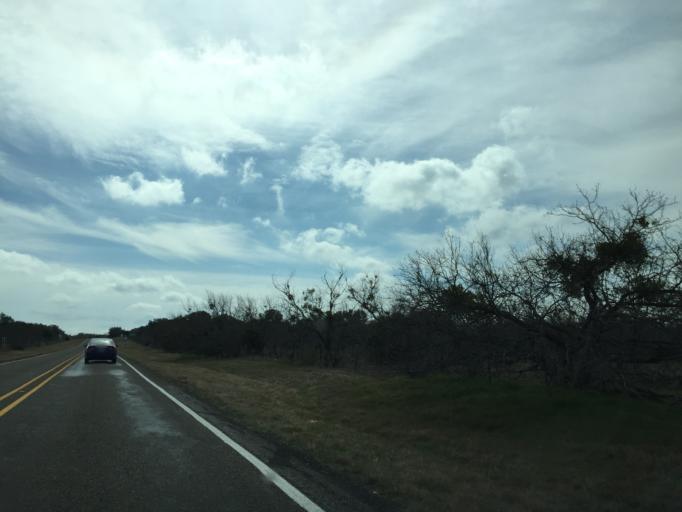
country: US
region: Texas
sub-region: Burnet County
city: Granite Shoals
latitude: 30.5033
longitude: -98.4411
